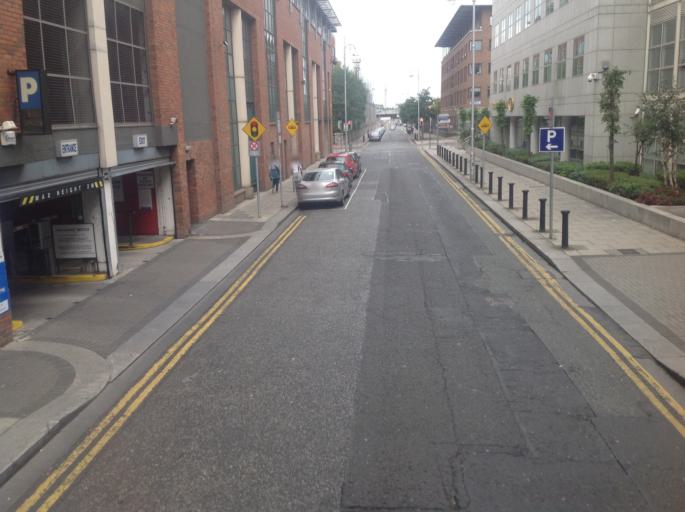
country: IE
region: Leinster
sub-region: Dublin City
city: Dublin
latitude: 53.3486
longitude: -6.2460
